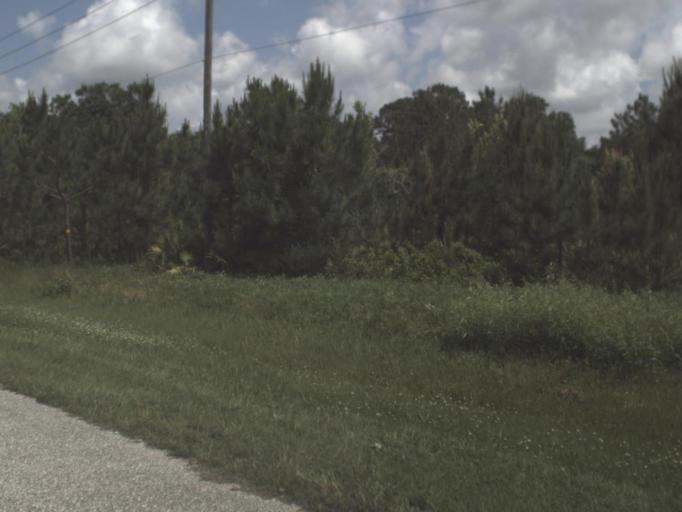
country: US
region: Florida
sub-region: Saint Johns County
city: Palm Valley
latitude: 30.0818
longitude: -81.4555
